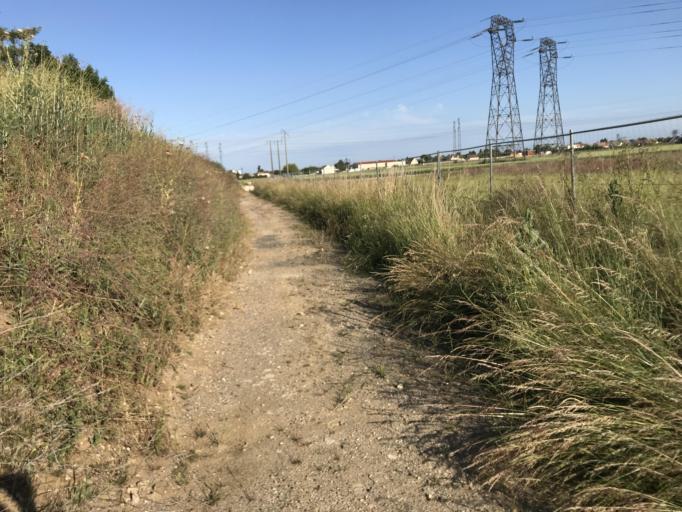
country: FR
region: Ile-de-France
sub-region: Departement de l'Essonne
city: Villejust
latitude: 48.6799
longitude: 2.2107
